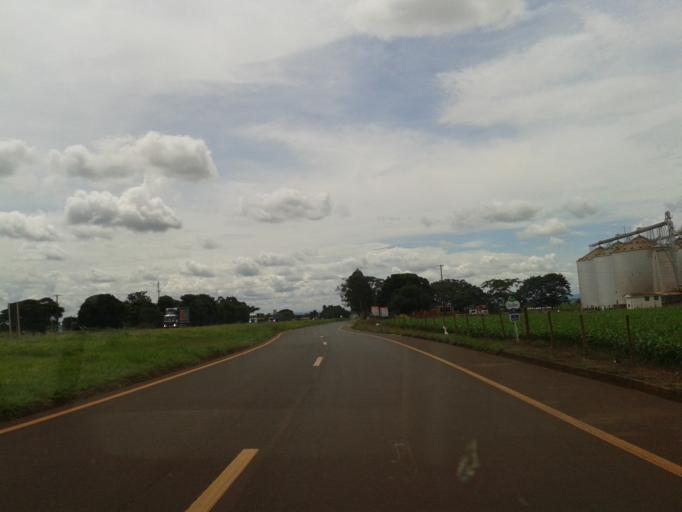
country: BR
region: Minas Gerais
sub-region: Centralina
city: Centralina
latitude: -18.5968
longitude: -49.1923
